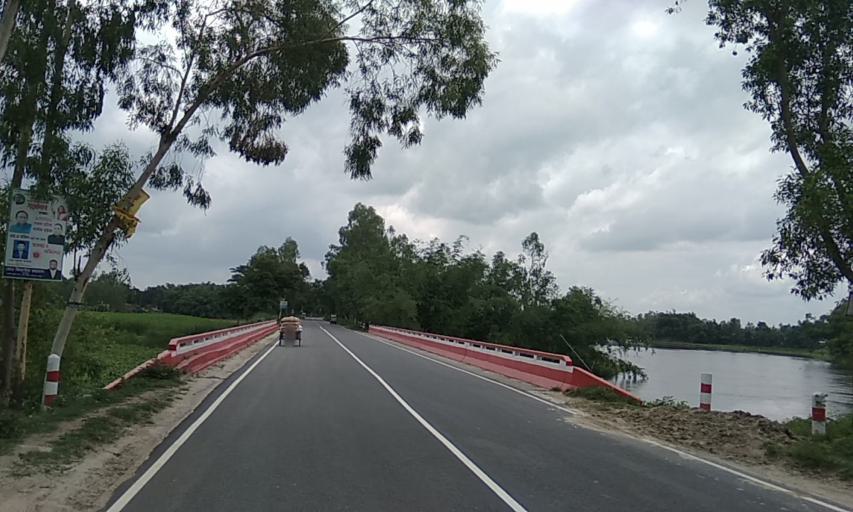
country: BD
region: Rangpur Division
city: Rangpur
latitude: 25.8018
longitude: 89.1844
